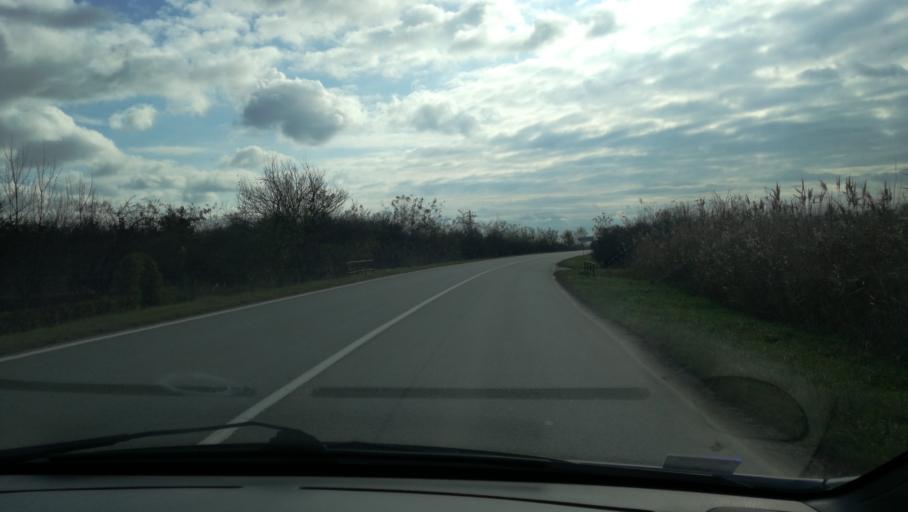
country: RS
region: Autonomna Pokrajina Vojvodina
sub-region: Severnobanatski Okrug
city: Kikinda
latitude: 45.8000
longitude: 20.4391
